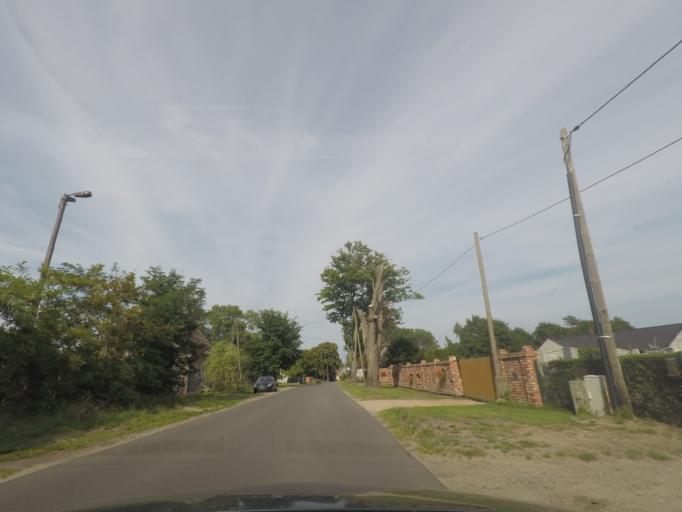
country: PL
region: Pomeranian Voivodeship
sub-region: Powiat slupski
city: Smoldzino
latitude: 54.6308
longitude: 17.1465
